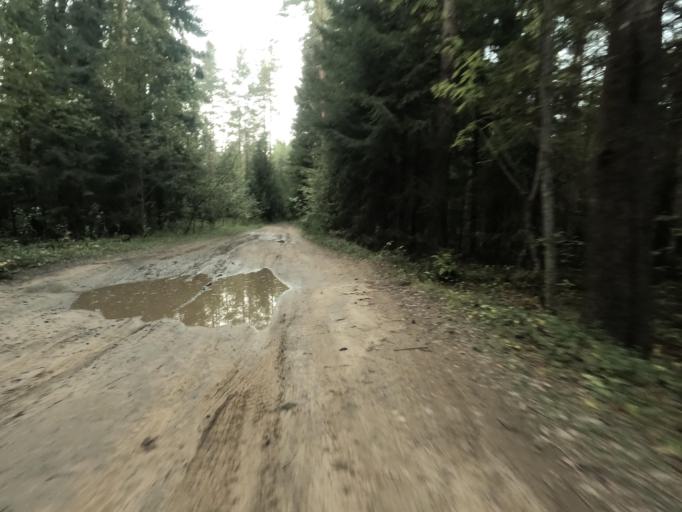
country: RU
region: Leningrad
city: Otradnoye
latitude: 59.8473
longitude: 30.7971
